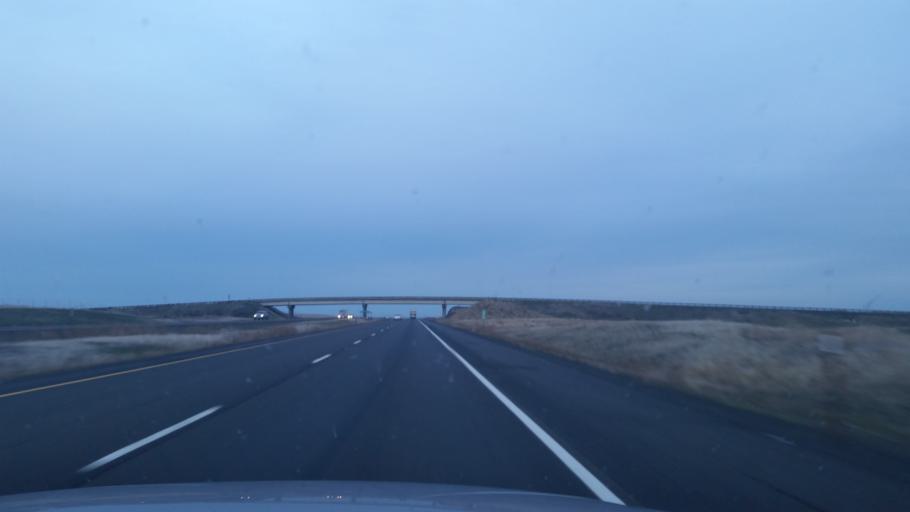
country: US
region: Washington
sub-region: Adams County
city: Ritzville
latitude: 47.2325
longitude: -118.1549
